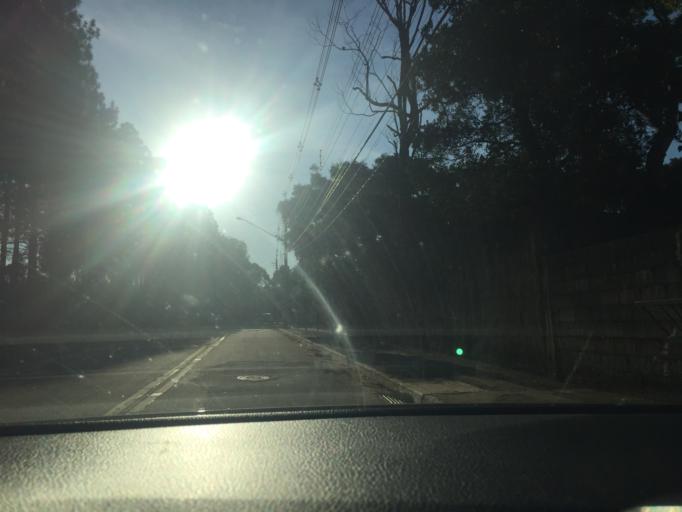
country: BR
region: Sao Paulo
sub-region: Louveira
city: Louveira
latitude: -23.1091
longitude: -46.9190
